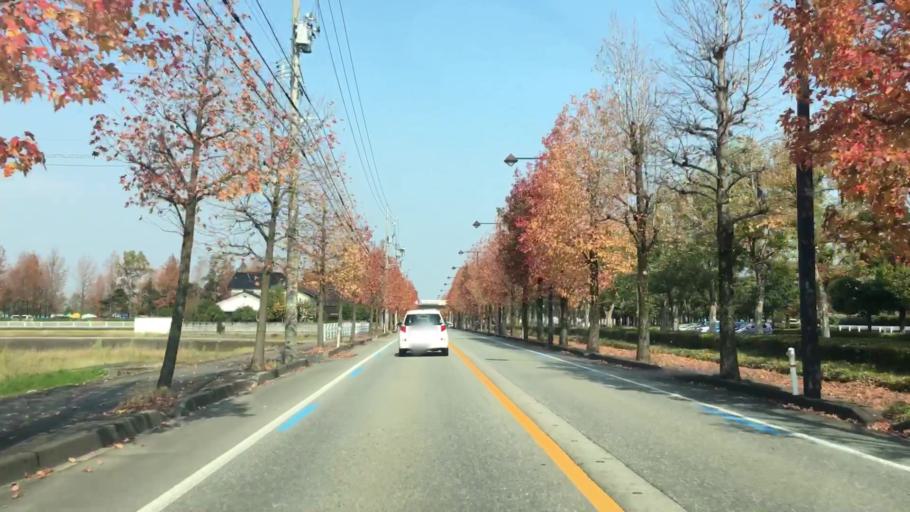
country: JP
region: Toyama
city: Toyama-shi
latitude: 36.6244
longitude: 137.1934
